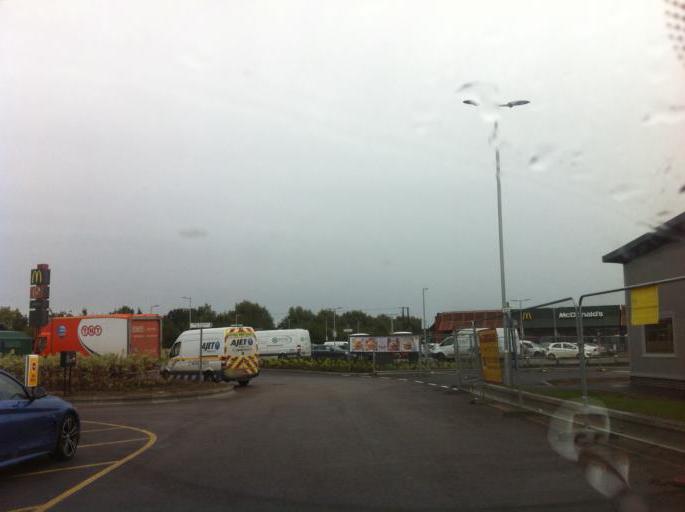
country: GB
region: England
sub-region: Lincolnshire
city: Kirton
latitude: 52.8893
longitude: -0.0856
